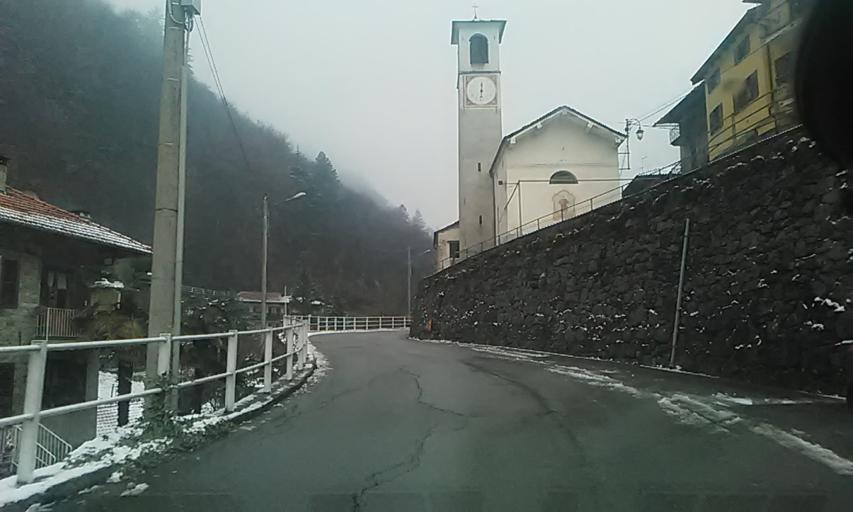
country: IT
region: Piedmont
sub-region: Provincia di Vercelli
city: Varallo
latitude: 45.8178
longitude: 8.2710
